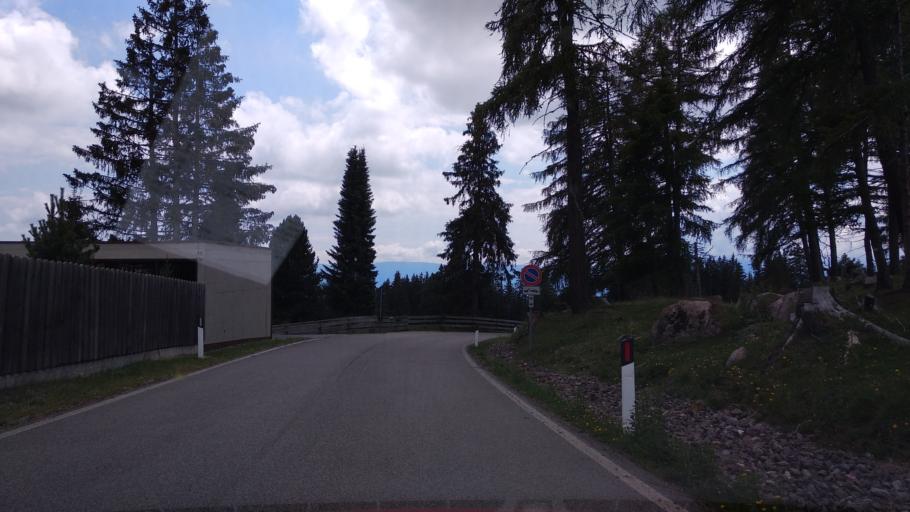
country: IT
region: Trentino-Alto Adige
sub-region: Bolzano
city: Avelengo
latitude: 46.6628
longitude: 11.2360
